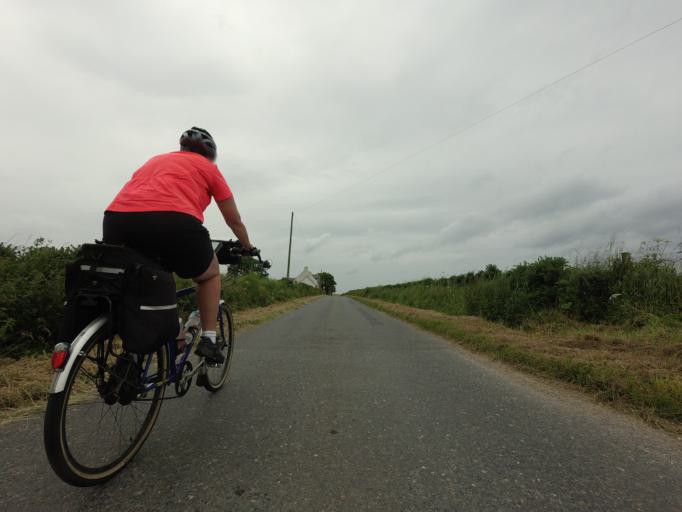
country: GB
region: Scotland
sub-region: Aberdeenshire
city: Portsoy
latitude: 57.6628
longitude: -2.7534
